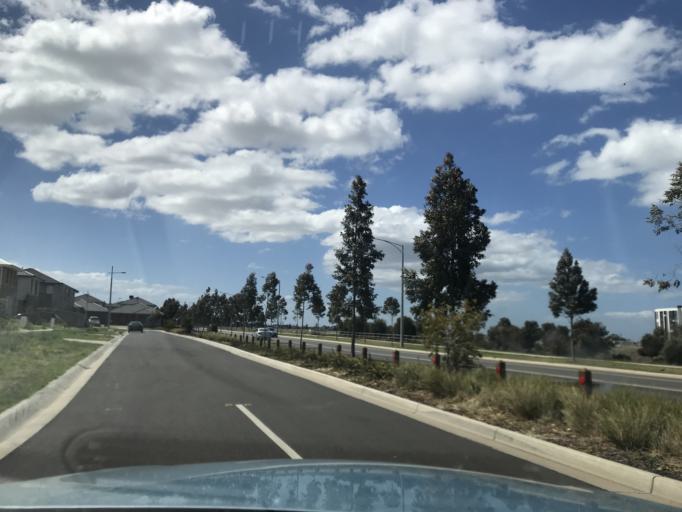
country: AU
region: Victoria
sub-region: Wyndham
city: Williams Landing
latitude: -37.8647
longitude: 144.7400
